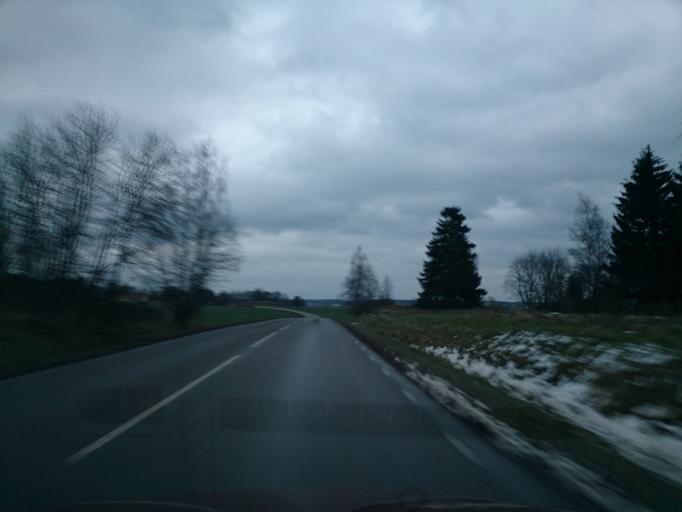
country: SE
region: OEstergoetland
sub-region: Linkopings Kommun
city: Sturefors
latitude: 58.3849
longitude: 15.7371
